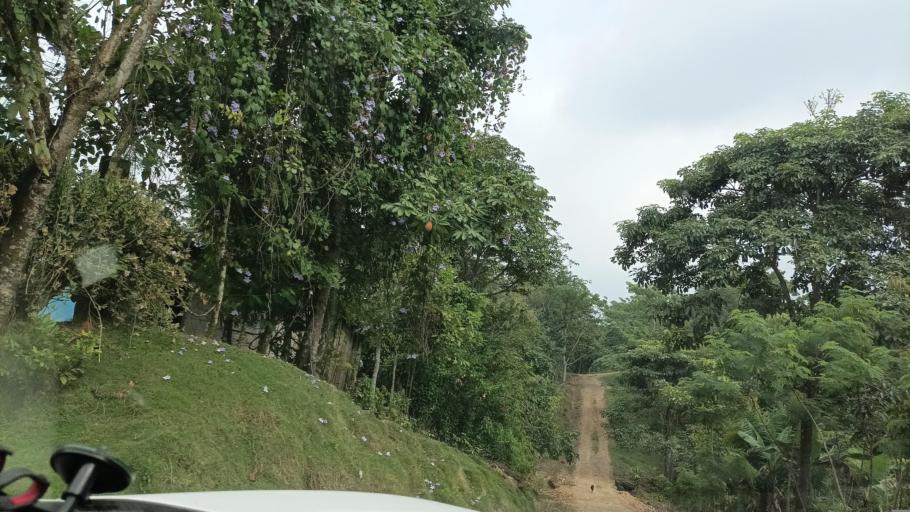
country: MX
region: Veracruz
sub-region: Moloacan
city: Cuichapa
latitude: 17.5777
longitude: -94.2286
